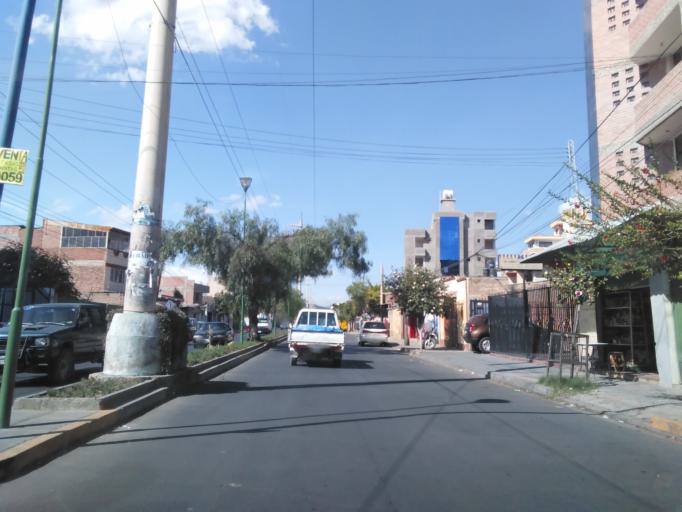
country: BO
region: Cochabamba
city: Cochabamba
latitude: -17.3964
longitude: -66.1785
